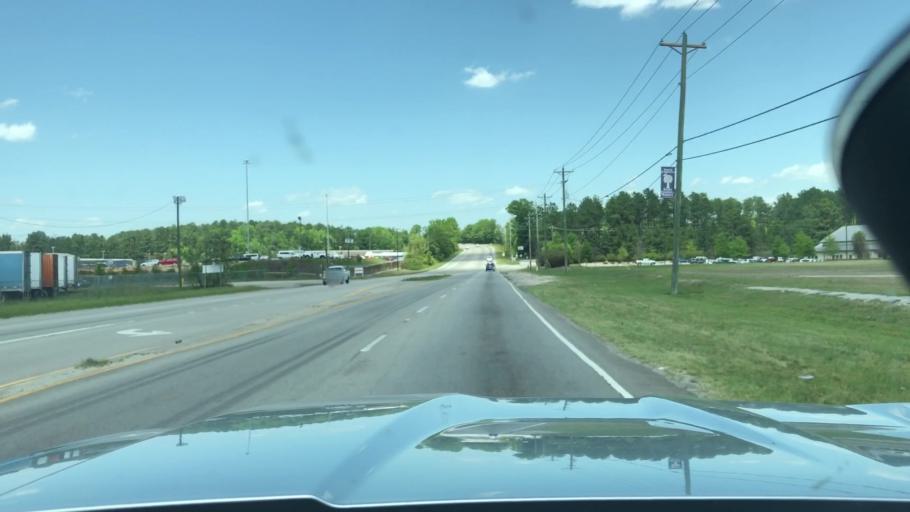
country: US
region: South Carolina
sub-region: Lexington County
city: Pineridge
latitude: 33.9034
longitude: -81.0650
